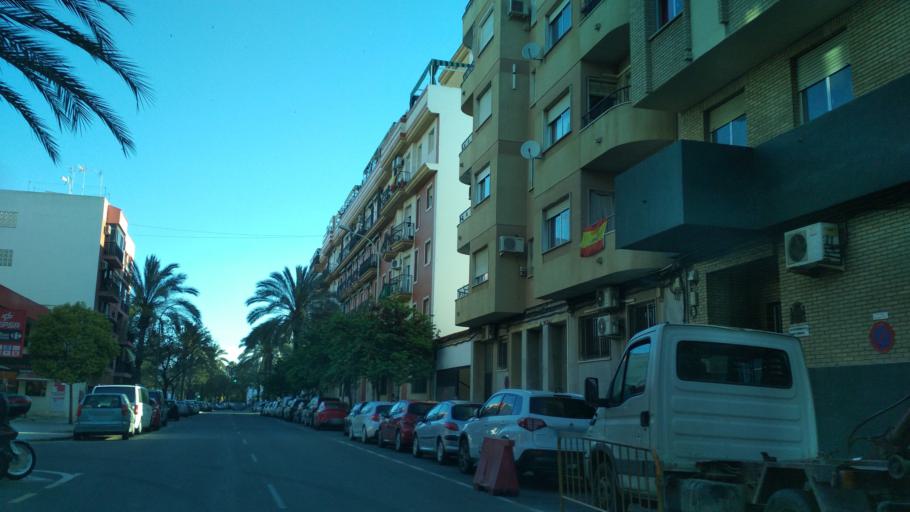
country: ES
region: Andalusia
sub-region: Provincia de Huelva
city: Huelva
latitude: 37.2663
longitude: -6.9521
